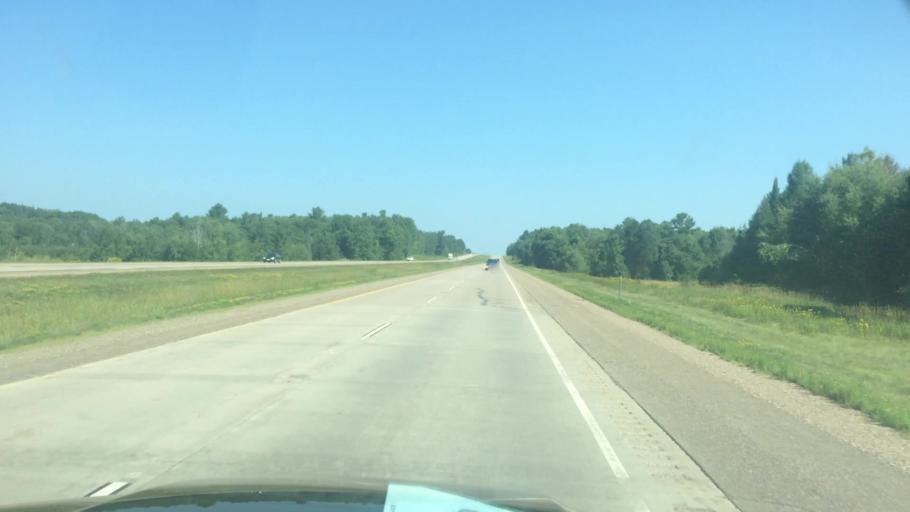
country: US
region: Wisconsin
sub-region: Lincoln County
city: Tomahawk
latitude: 45.3413
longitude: -89.6646
